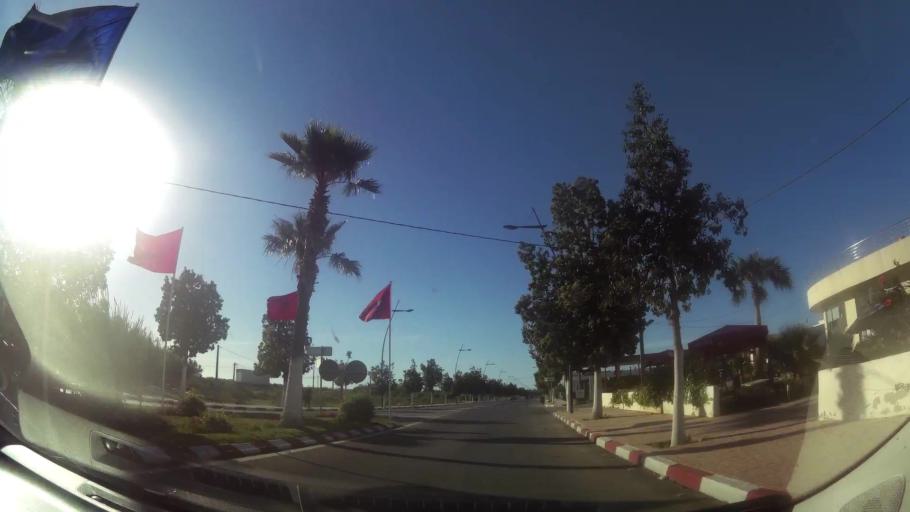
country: MA
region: Oriental
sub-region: Berkane-Taourirt
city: Madagh
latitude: 35.0677
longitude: -2.2164
